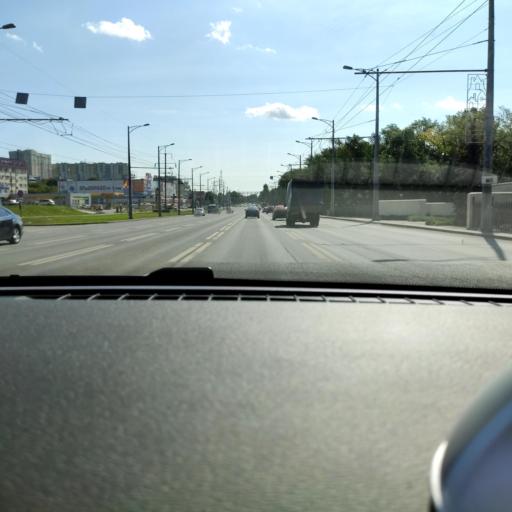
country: RU
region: Samara
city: Samara
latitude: 53.2156
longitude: 50.1803
